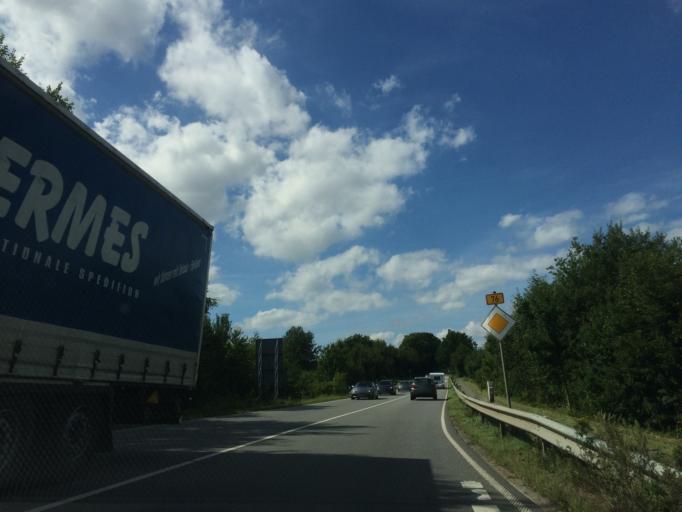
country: DE
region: Schleswig-Holstein
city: Eutin
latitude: 54.1290
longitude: 10.5714
